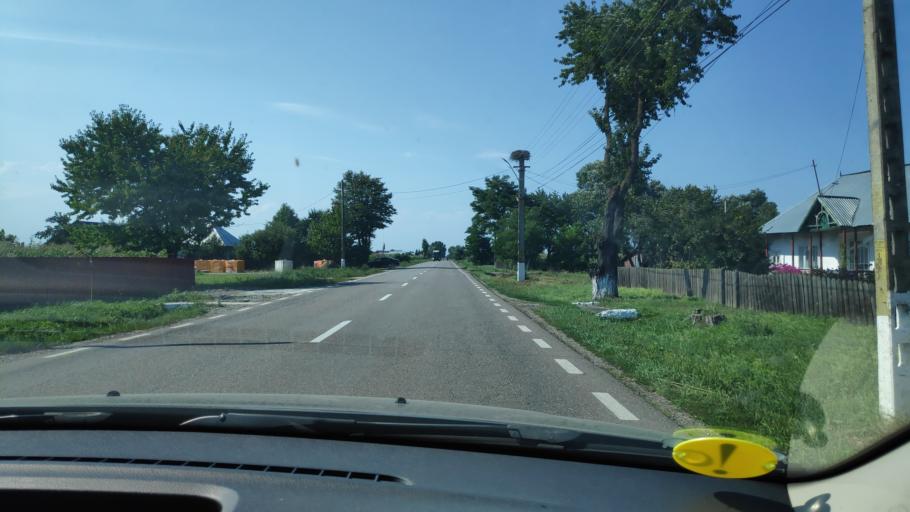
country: RO
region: Suceava
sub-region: Comuna Boroaia
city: Boroaia
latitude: 47.3698
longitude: 26.3301
